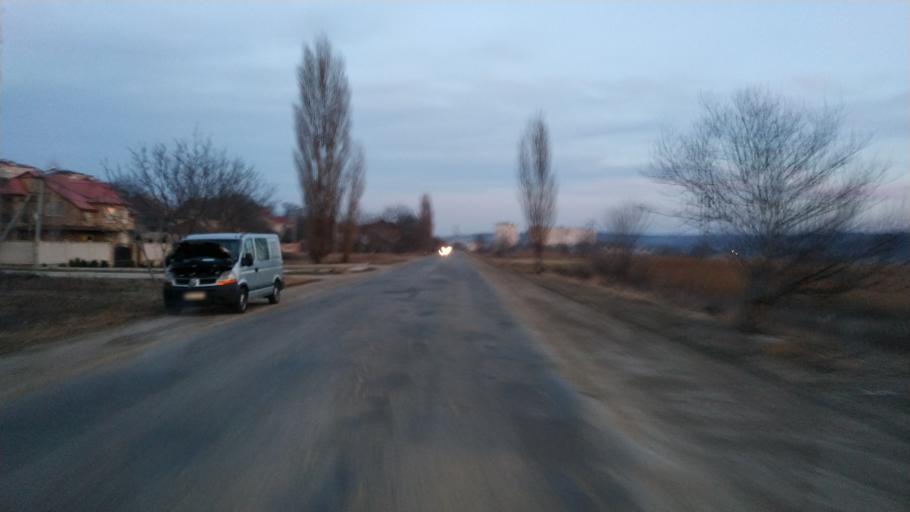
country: MD
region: Laloveni
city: Ialoveni
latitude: 46.9479
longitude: 28.7697
